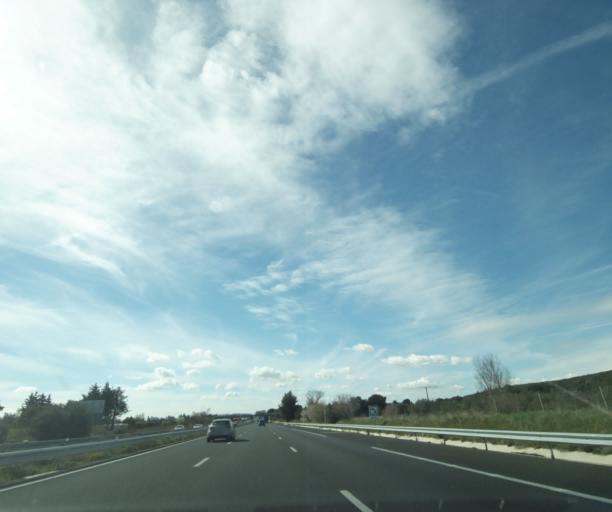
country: FR
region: Languedoc-Roussillon
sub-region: Departement du Gard
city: Marguerittes
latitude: 43.8642
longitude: 4.4331
